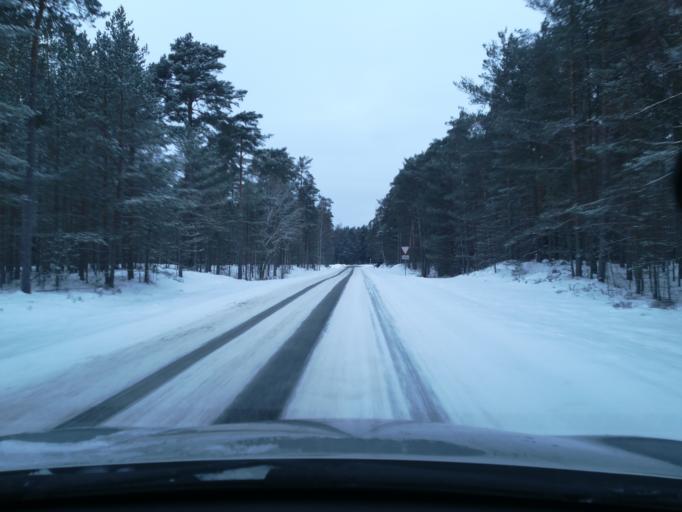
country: EE
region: Harju
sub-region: Keila linn
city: Keila
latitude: 59.3907
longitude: 24.2949
